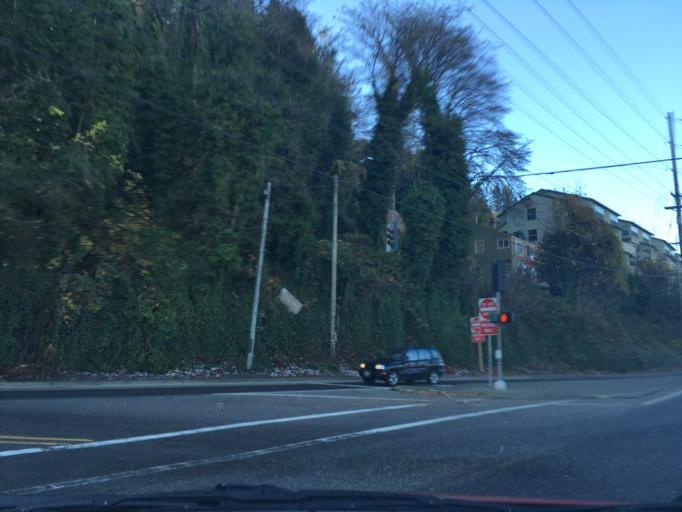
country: US
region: Oregon
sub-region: Washington County
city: West Haven
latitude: 45.5875
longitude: -122.7736
